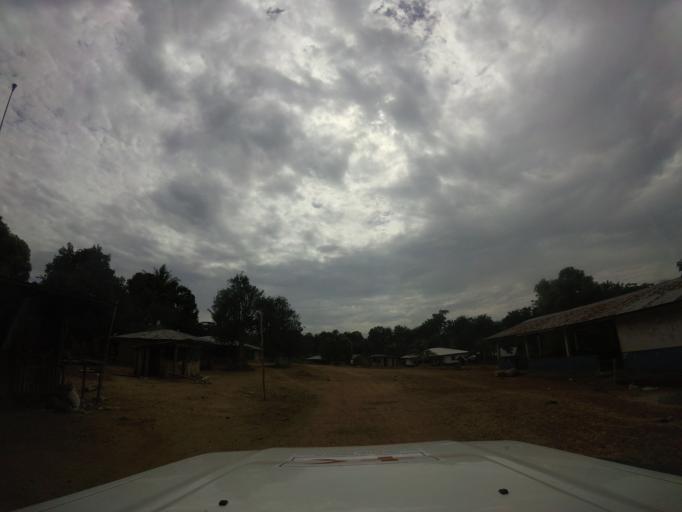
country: SL
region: Southern Province
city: Zimmi
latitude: 7.1834
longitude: -11.2313
